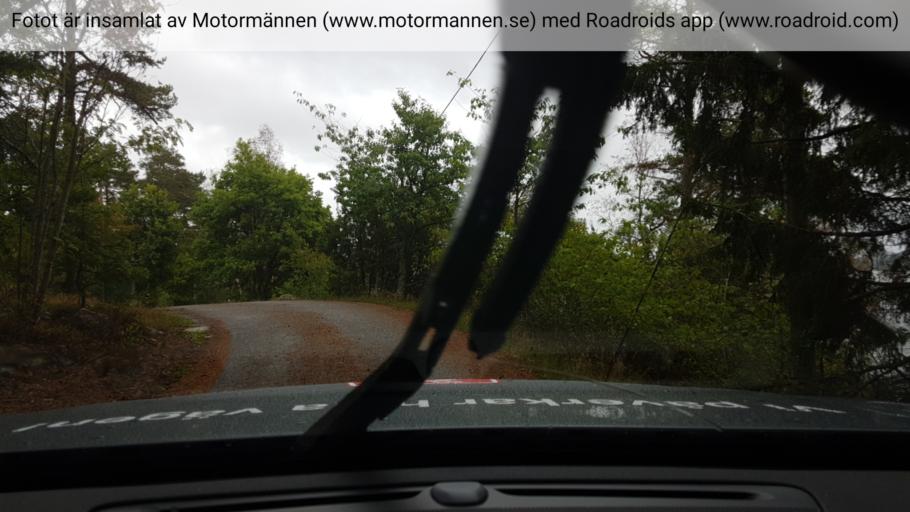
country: SE
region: Stockholm
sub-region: Haninge Kommun
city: Jordbro
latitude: 59.0220
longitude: 18.0986
